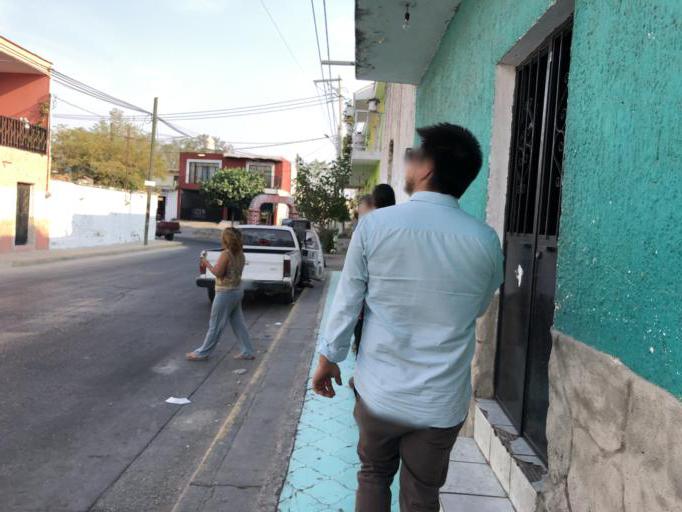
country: MX
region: Jalisco
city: Tlaquepaque
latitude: 20.6021
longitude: -103.2891
